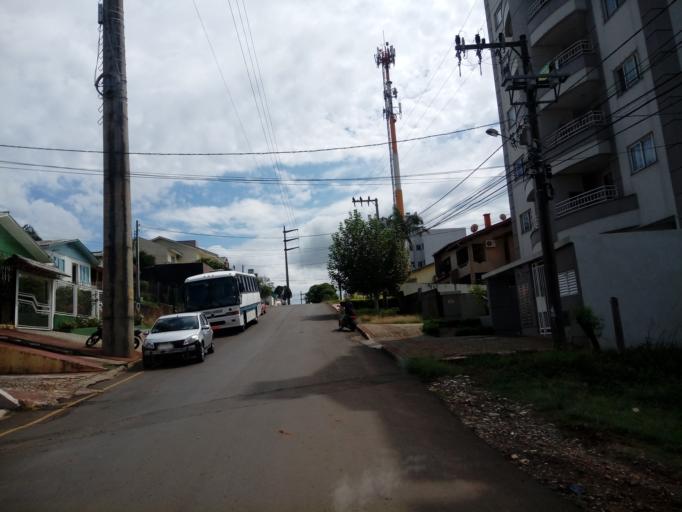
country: BR
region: Santa Catarina
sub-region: Chapeco
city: Chapeco
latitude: -27.1046
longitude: -52.6002
